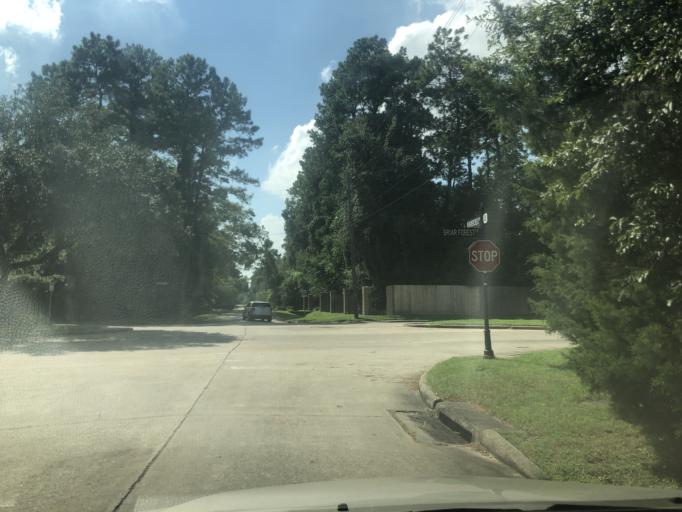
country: US
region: Texas
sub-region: Harris County
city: Bunker Hill Village
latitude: 29.7478
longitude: -95.5460
